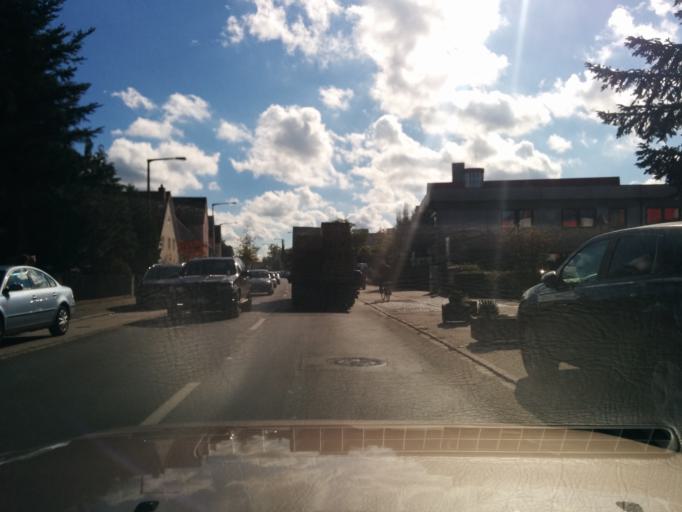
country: DE
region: Bavaria
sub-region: Regierungsbezirk Mittelfranken
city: Nuernberg
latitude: 49.4879
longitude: 11.1039
